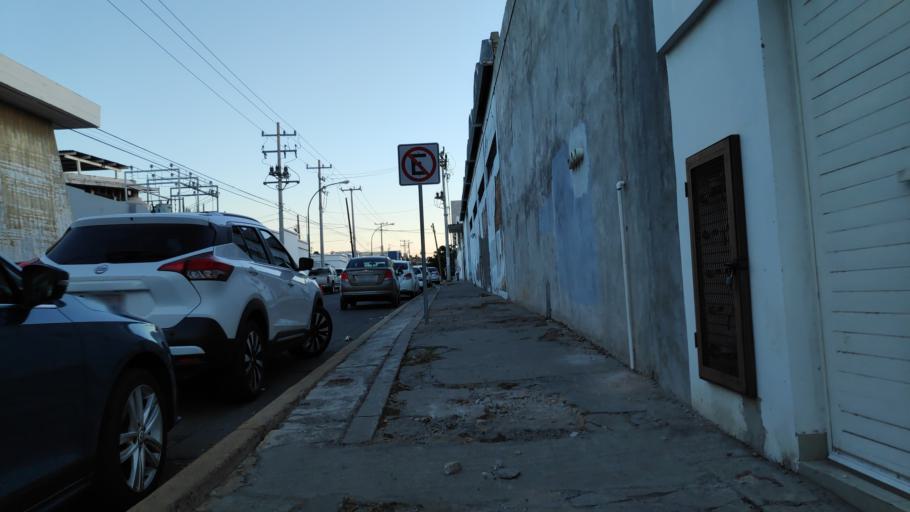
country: MX
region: Sinaloa
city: Culiacan
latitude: 24.7974
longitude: -107.3926
